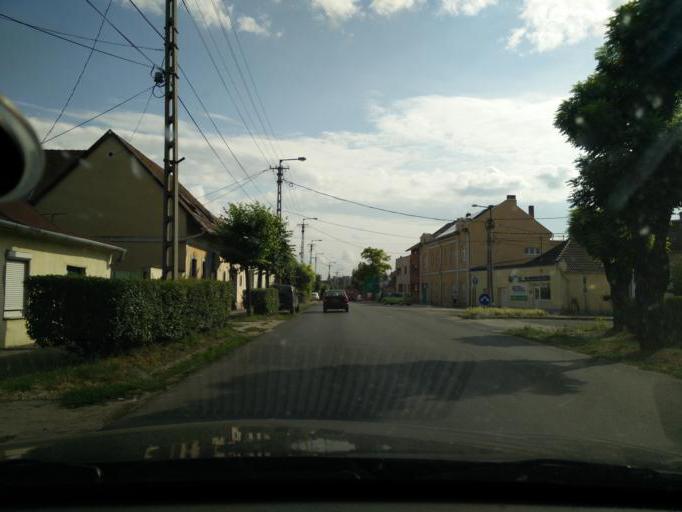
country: HU
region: Komarom-Esztergom
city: Tata
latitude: 47.6549
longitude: 18.3261
